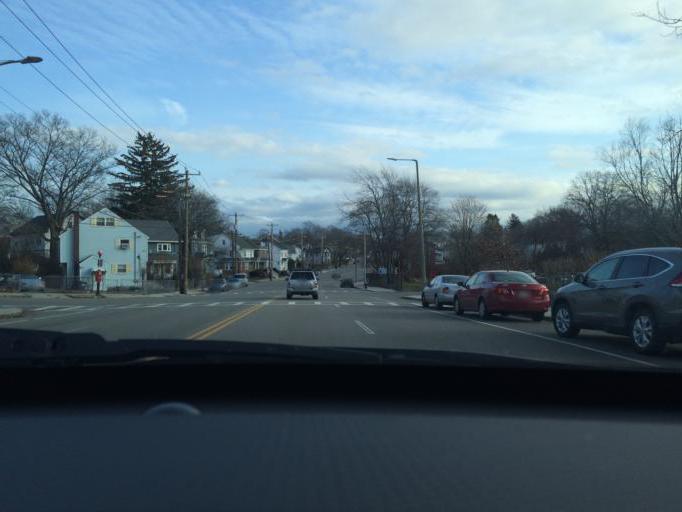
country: US
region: Massachusetts
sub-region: Norfolk County
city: Milton
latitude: 42.2761
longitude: -71.0745
